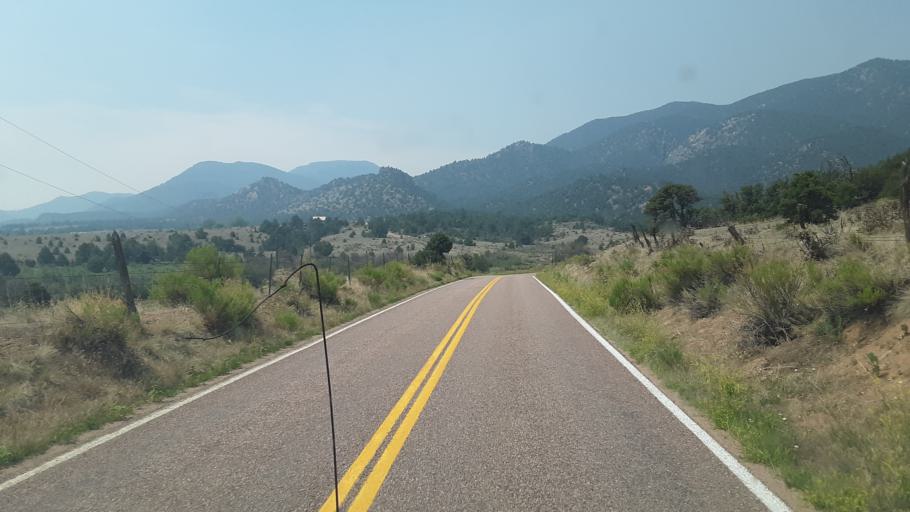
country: US
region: Colorado
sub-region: Fremont County
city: Canon City
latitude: 38.4362
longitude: -105.3804
